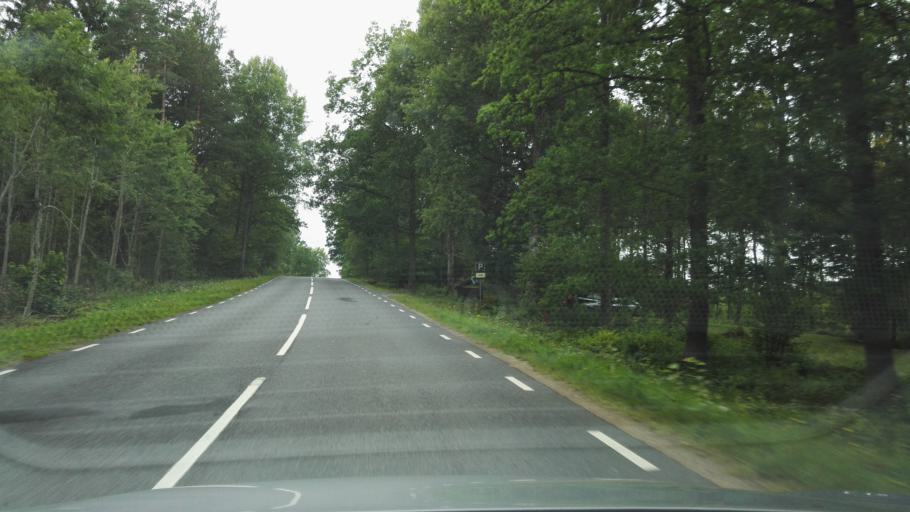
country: SE
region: Joenkoeping
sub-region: Vetlanda Kommun
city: Landsbro
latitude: 57.3120
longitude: 14.8695
